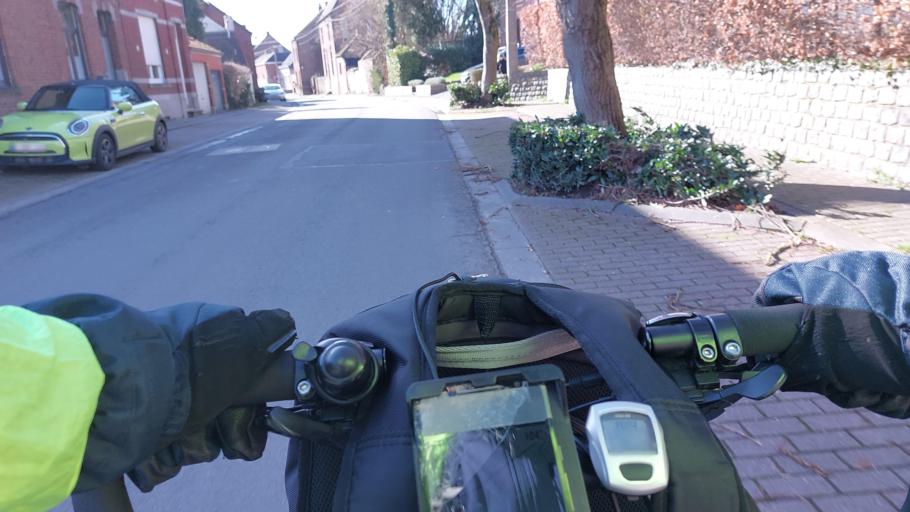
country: BE
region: Wallonia
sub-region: Province du Hainaut
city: Seneffe
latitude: 50.5660
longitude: 4.2530
